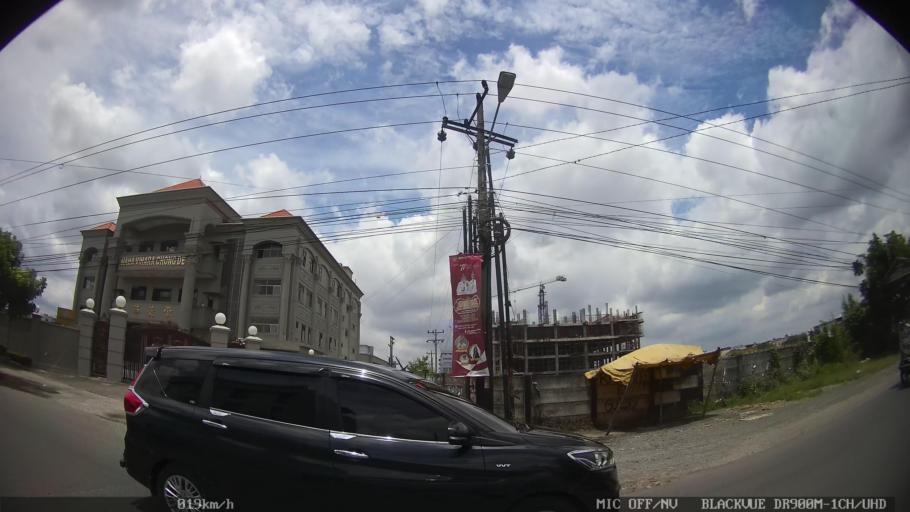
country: ID
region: North Sumatra
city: Medan
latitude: 3.6002
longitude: 98.7118
